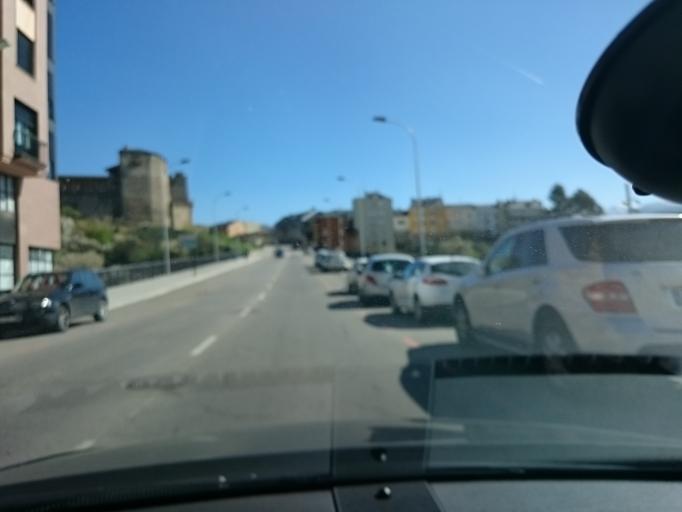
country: ES
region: Castille and Leon
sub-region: Provincia de Leon
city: Ponferrada
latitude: 42.5444
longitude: -6.5961
